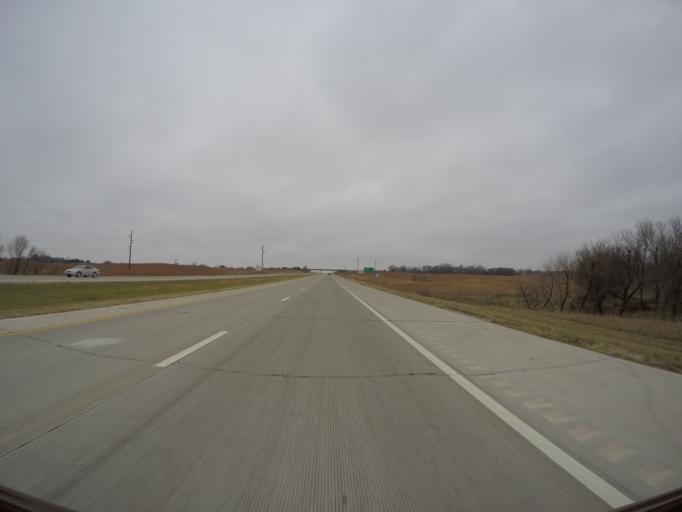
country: US
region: Kansas
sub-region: Dickinson County
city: Abilene
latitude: 38.9531
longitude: -97.1248
